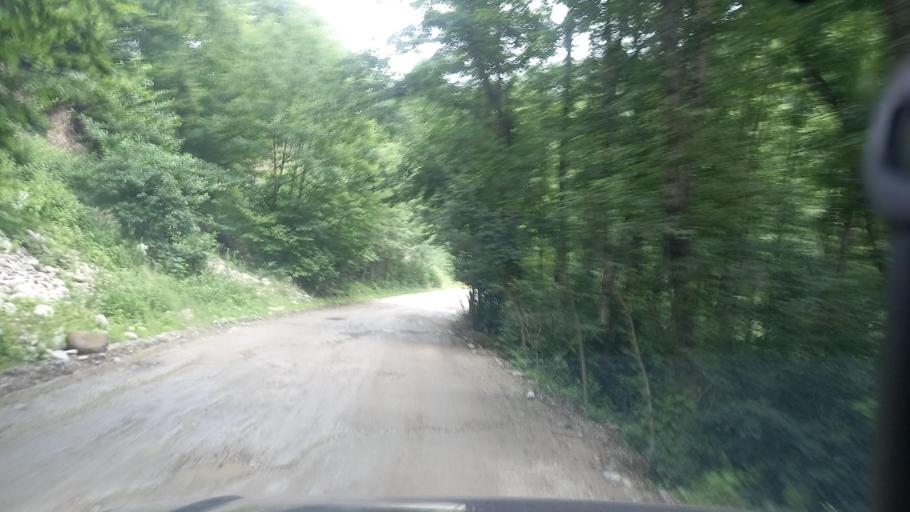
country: RU
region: Karachayevo-Cherkesiya
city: Kurdzhinovo
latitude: 43.8876
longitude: 40.9493
